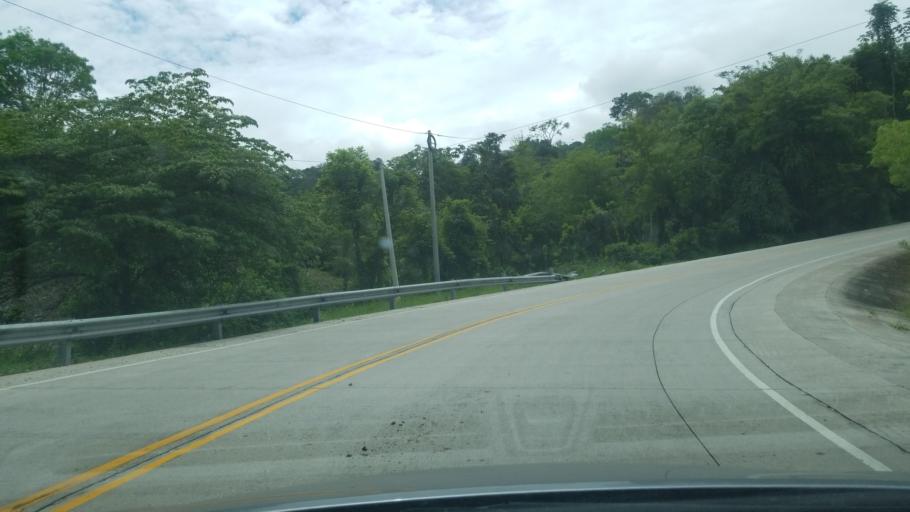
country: HN
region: Copan
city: Florida
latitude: 14.9974
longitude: -88.8437
